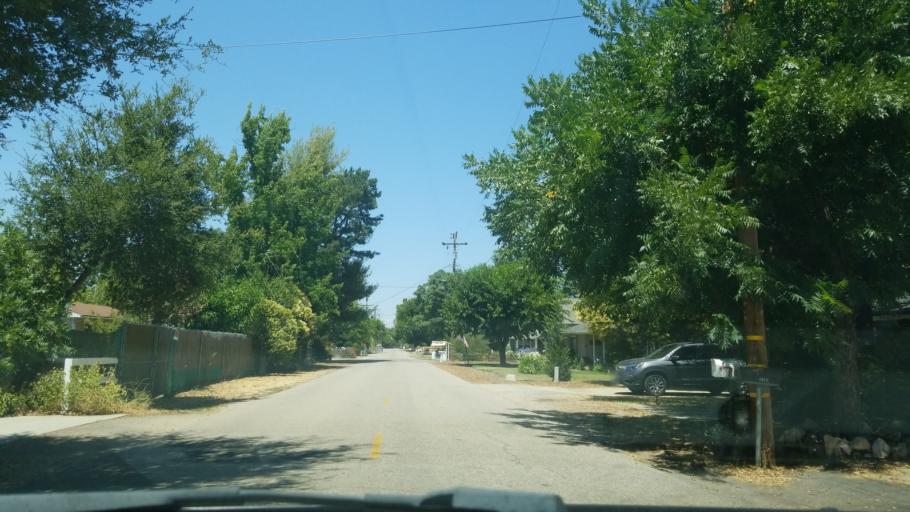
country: US
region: California
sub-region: San Luis Obispo County
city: Atascadero
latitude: 35.5049
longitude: -120.6634
